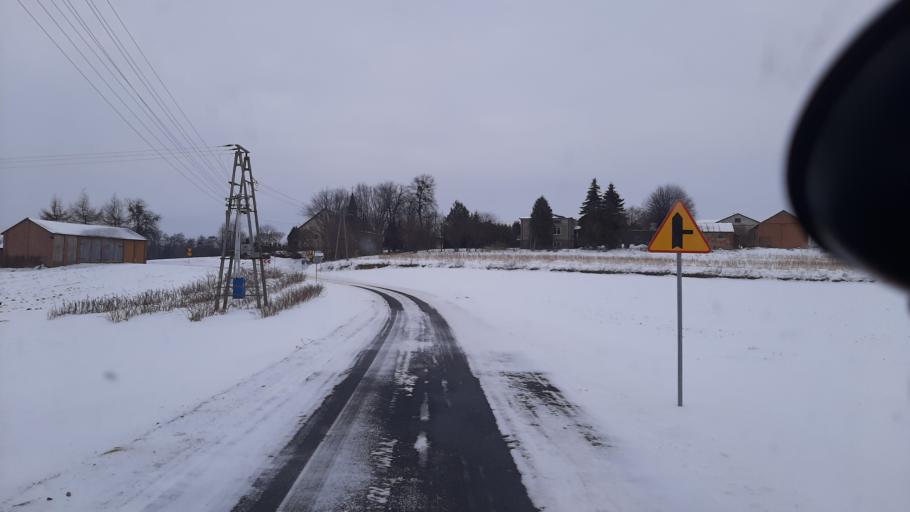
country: PL
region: Lublin Voivodeship
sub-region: Powiat lubelski
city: Garbow
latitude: 51.3412
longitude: 22.2933
